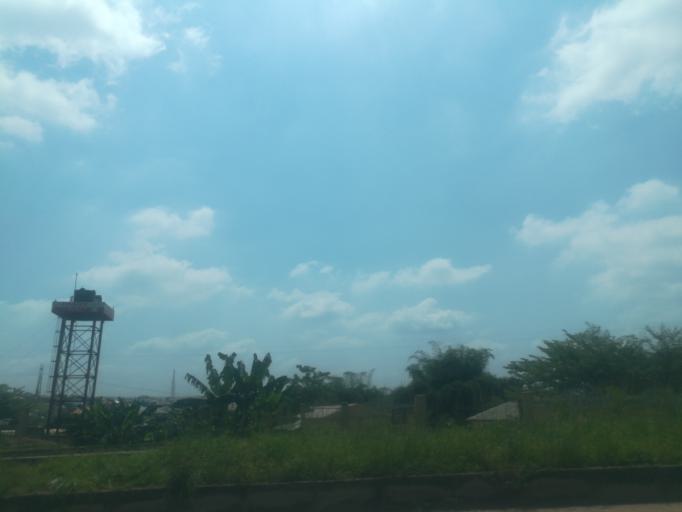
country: NG
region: Ogun
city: Abeokuta
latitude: 7.1426
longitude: 3.3864
